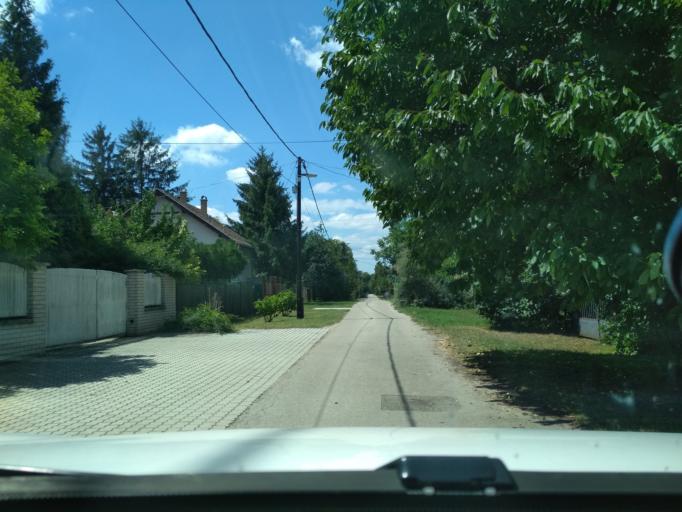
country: HU
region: Fejer
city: Gardony
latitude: 47.2116
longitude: 18.6534
